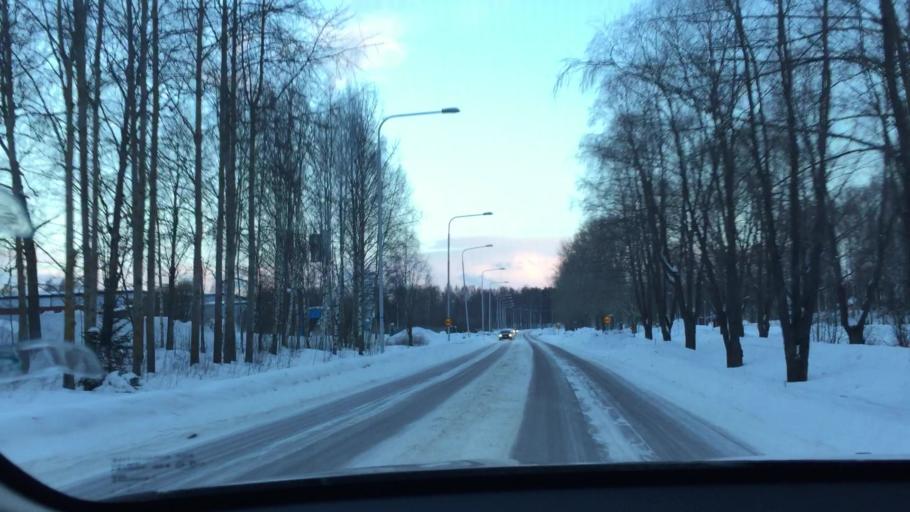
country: SE
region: Dalarna
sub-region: Faluns Kommun
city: Falun
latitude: 60.5872
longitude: 15.6528
